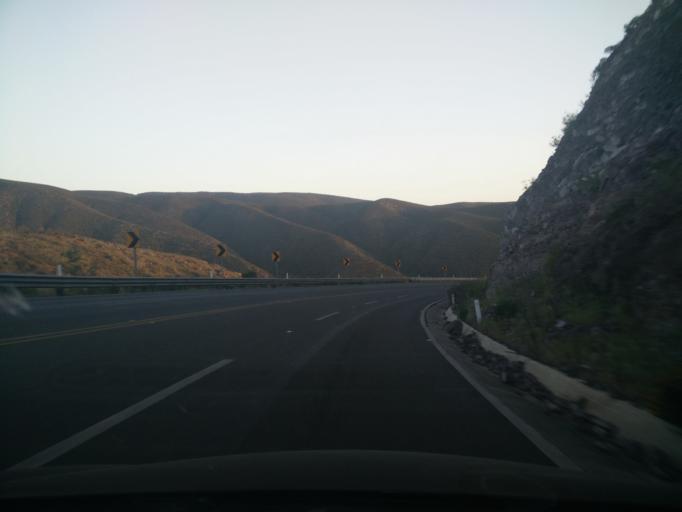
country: MX
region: Baja California
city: El Sauzal
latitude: 31.9305
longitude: -116.6675
